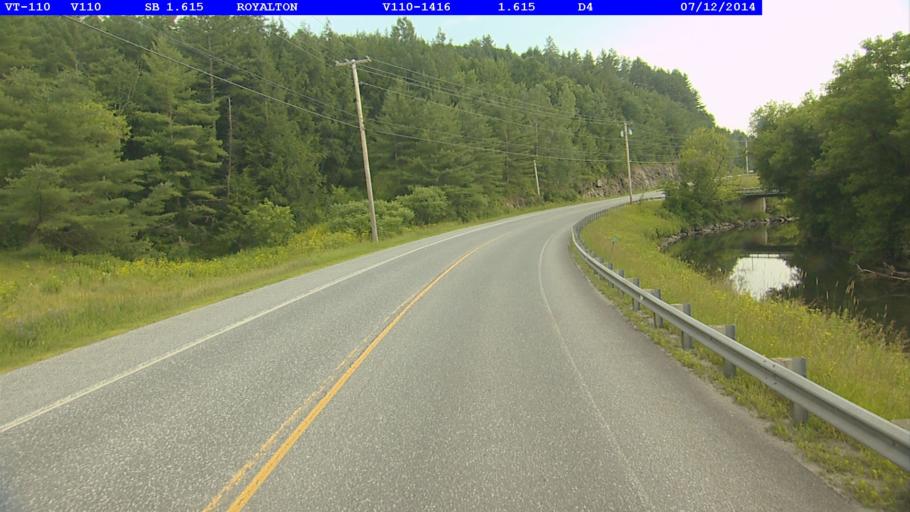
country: US
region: Vermont
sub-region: Orange County
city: Chelsea
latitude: 43.8437
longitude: -72.5111
